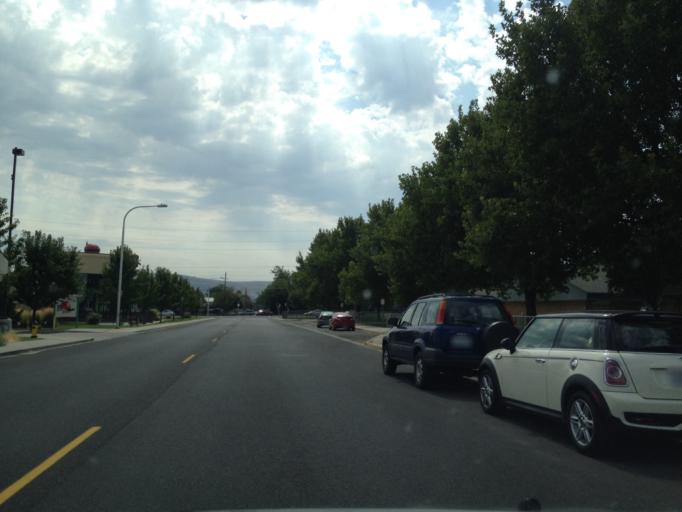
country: US
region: Washington
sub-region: Yakima County
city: West Valley
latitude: 46.5871
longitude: -120.5671
